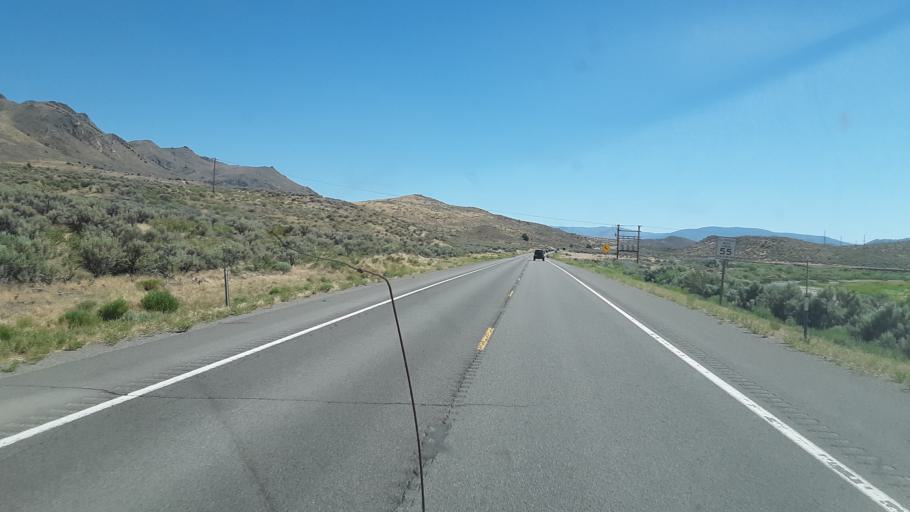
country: US
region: Nevada
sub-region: Washoe County
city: Cold Springs
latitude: 39.9016
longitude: -120.0142
